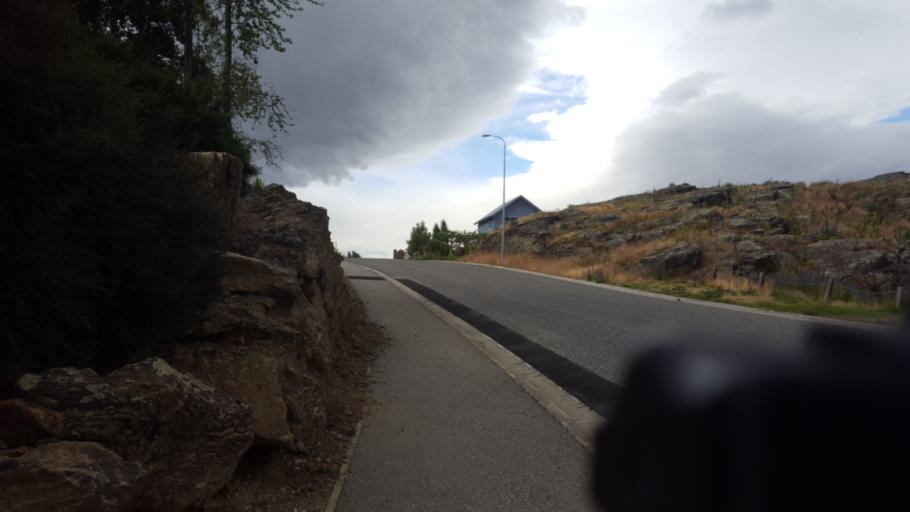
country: NZ
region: Otago
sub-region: Queenstown-Lakes District
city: Wanaka
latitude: -45.2518
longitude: 169.4030
